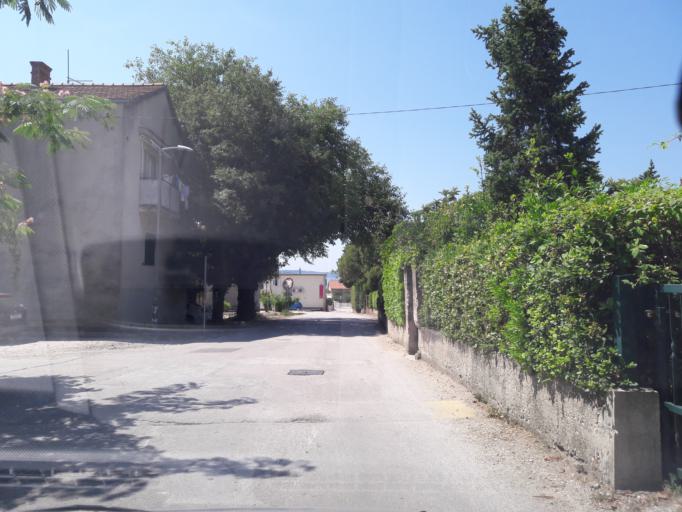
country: HR
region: Splitsko-Dalmatinska
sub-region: Grad Split
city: Split
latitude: 43.5500
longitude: 16.4002
